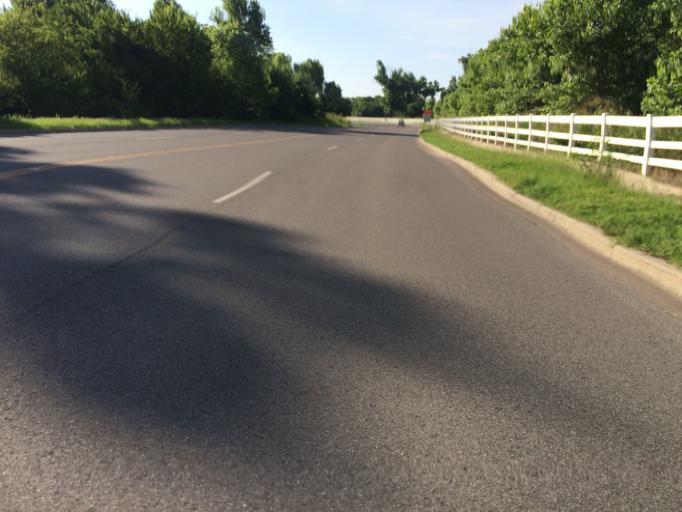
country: US
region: Oklahoma
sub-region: Cleveland County
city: Norman
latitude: 35.2056
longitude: -97.4897
